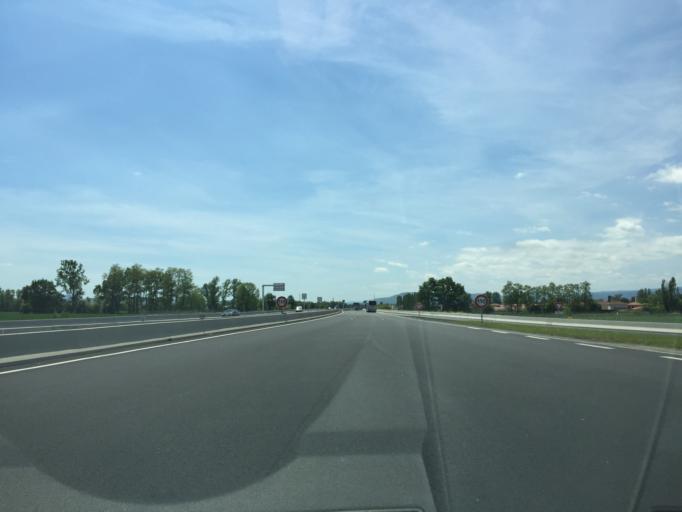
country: FR
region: Auvergne
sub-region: Departement du Puy-de-Dome
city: Gerzat
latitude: 45.8392
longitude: 3.1603
